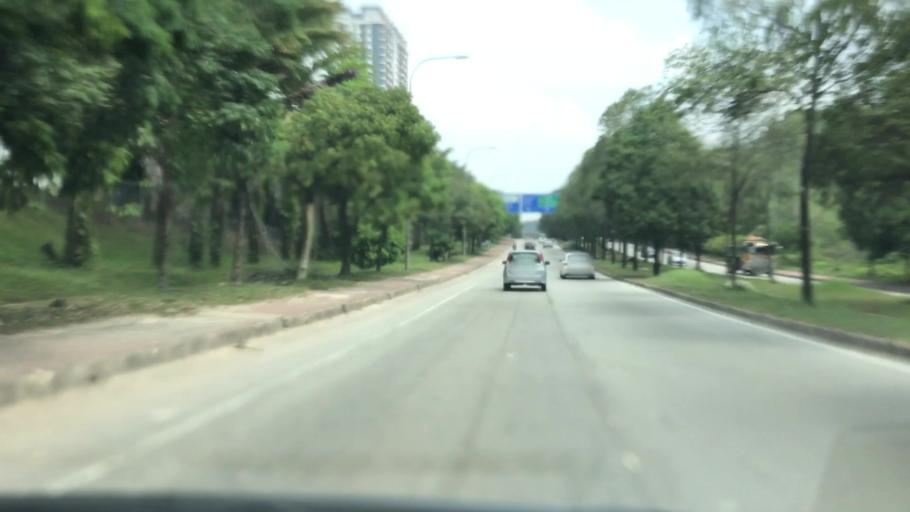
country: MY
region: Selangor
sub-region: Petaling
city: Petaling Jaya
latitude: 3.0559
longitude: 101.6635
